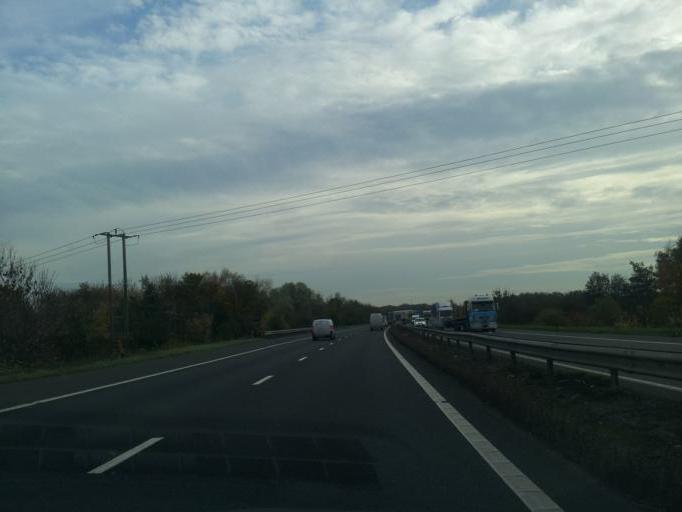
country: GB
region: England
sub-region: Cambridgeshire
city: Duxford
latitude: 52.1217
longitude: 0.1250
